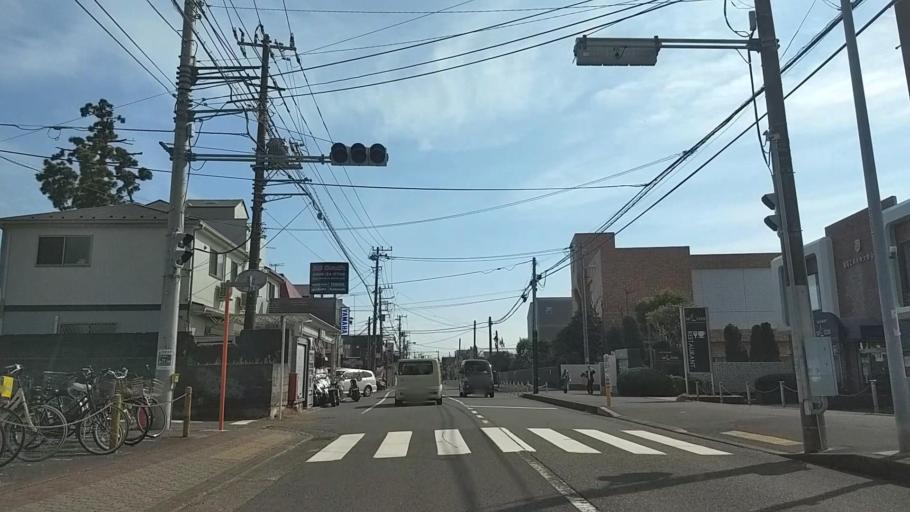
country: JP
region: Kanagawa
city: Fujisawa
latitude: 35.3264
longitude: 139.4532
